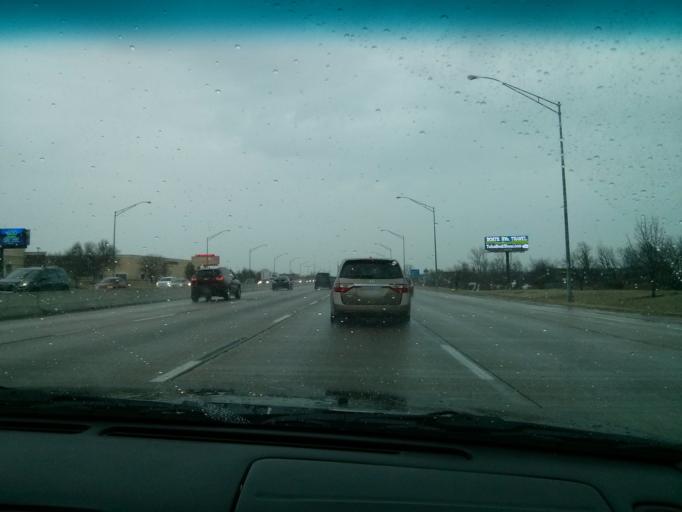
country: US
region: Oklahoma
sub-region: Tulsa County
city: Broken Arrow
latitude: 36.0652
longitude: -95.8593
